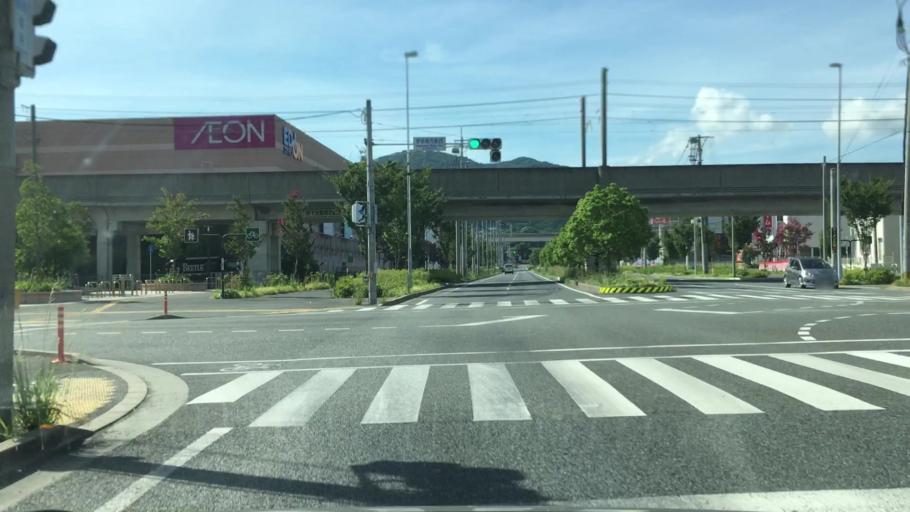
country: JP
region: Fukuoka
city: Maebaru-chuo
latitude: 33.5780
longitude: 130.2554
